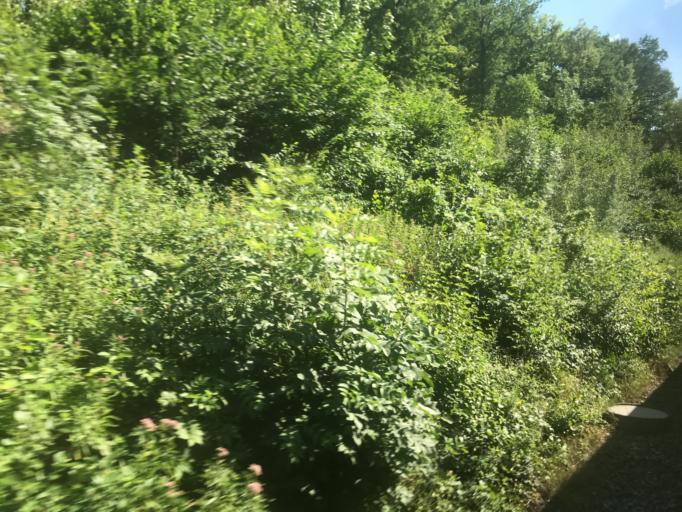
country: AT
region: Upper Austria
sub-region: Politischer Bezirk Urfahr-Umgebung
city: Engerwitzdorf
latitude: 48.3528
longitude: 14.5024
